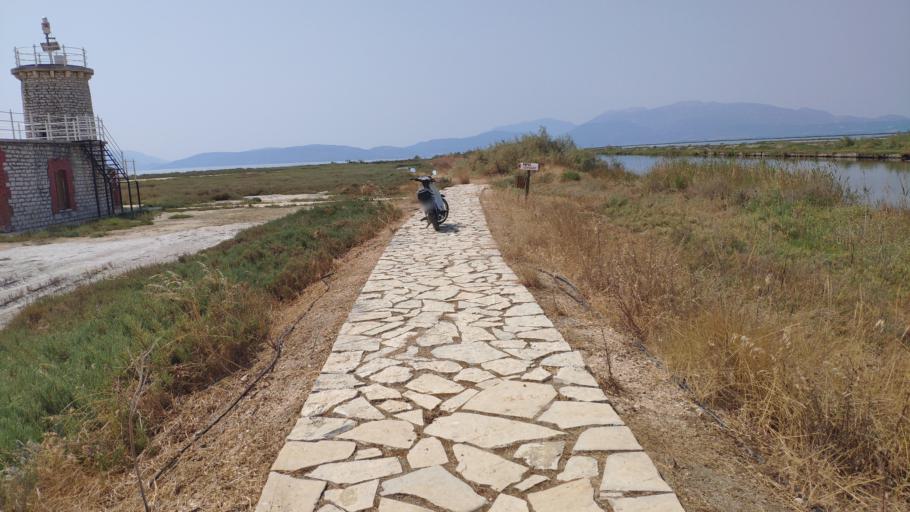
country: GR
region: West Greece
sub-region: Nomos Aitolias kai Akarnanias
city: Menidi
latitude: 39.0301
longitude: 21.0754
